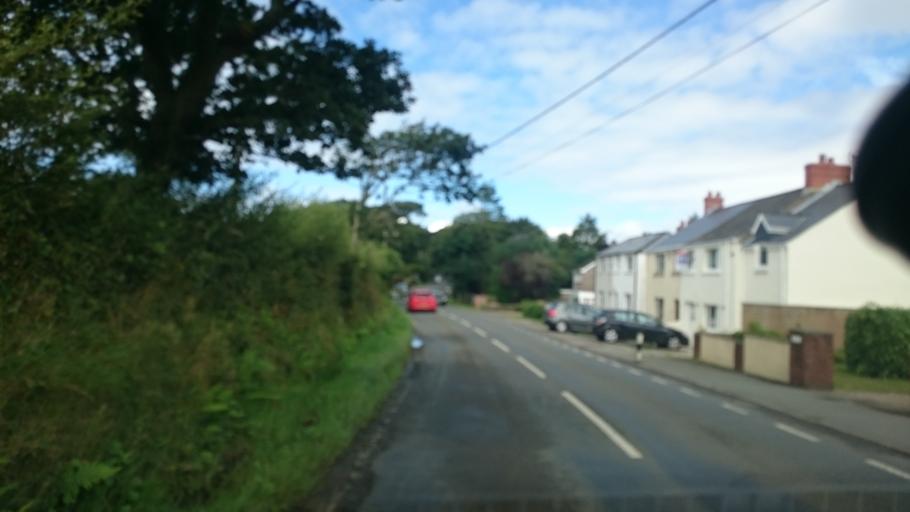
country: GB
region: Wales
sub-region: Pembrokeshire
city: Freystrop
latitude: 51.7609
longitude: -4.9597
